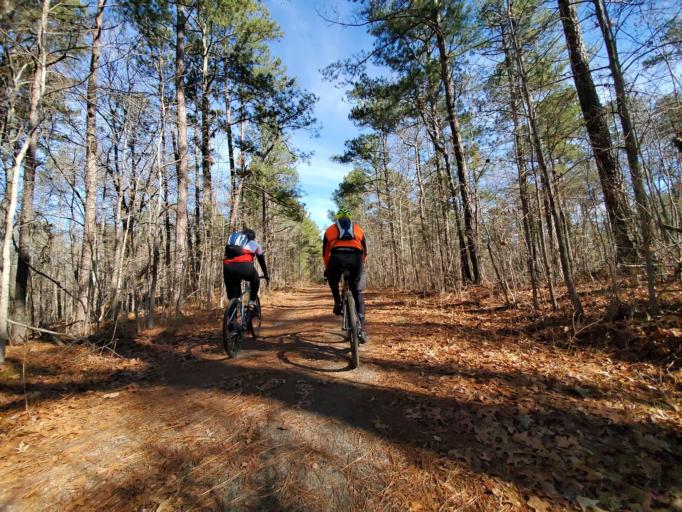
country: US
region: Georgia
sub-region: Fulton County
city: Chattahoochee Hills
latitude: 33.5679
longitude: -84.7494
